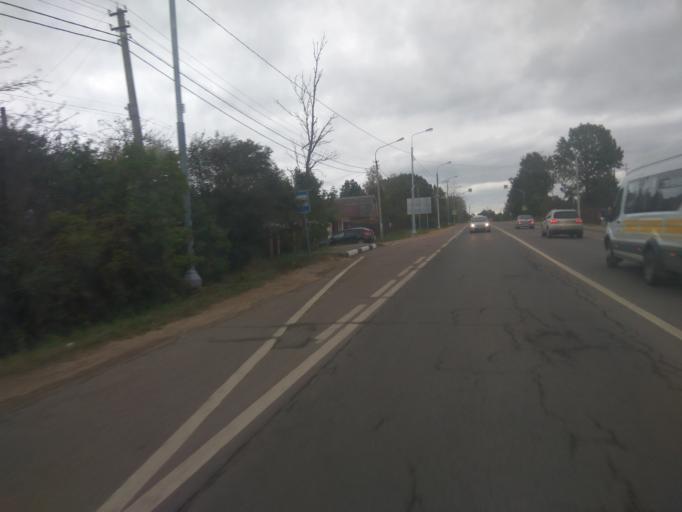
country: RU
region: Moskovskaya
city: Chupryakovo
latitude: 55.5731
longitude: 36.6540
